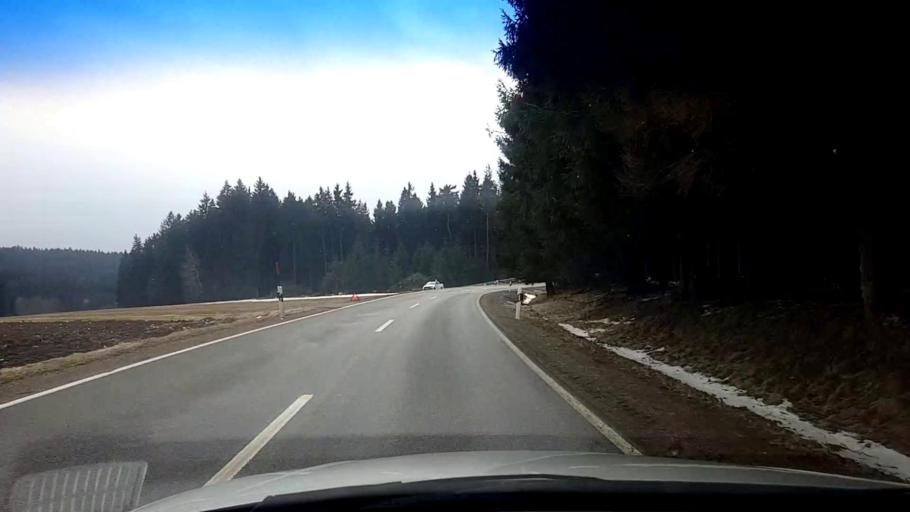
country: DE
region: Bavaria
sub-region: Upper Franconia
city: Stammbach
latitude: 50.1795
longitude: 11.7024
